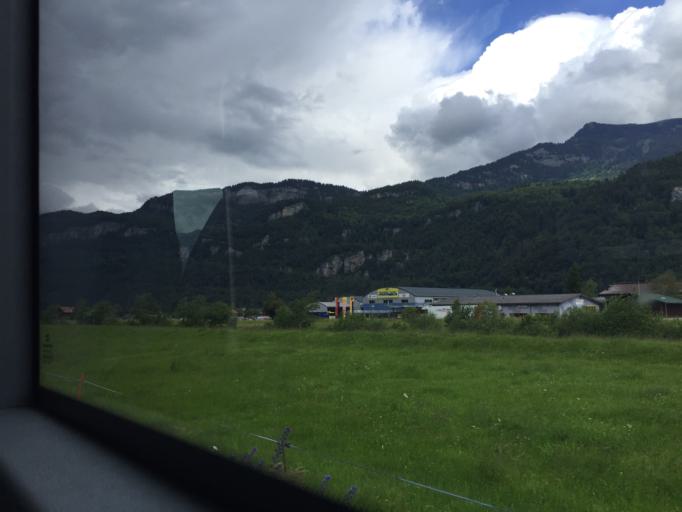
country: CH
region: Bern
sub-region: Interlaken-Oberhasli District
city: Meiringen
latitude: 46.7276
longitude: 8.1694
